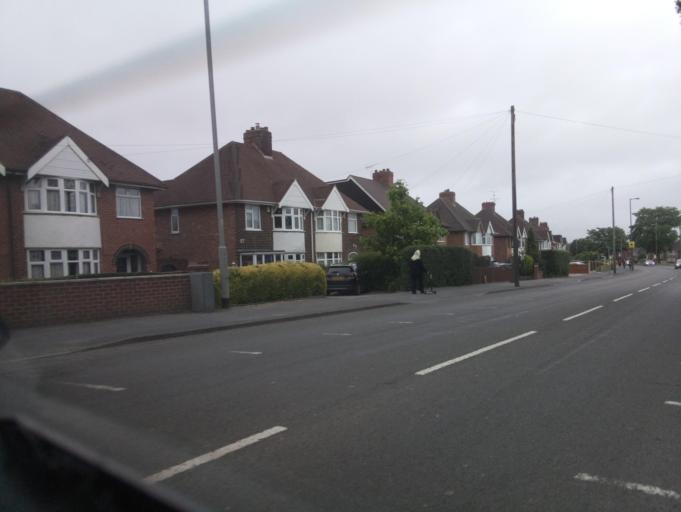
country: GB
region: England
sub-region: Staffordshire
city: Burton upon Trent
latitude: 52.7867
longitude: -1.6172
